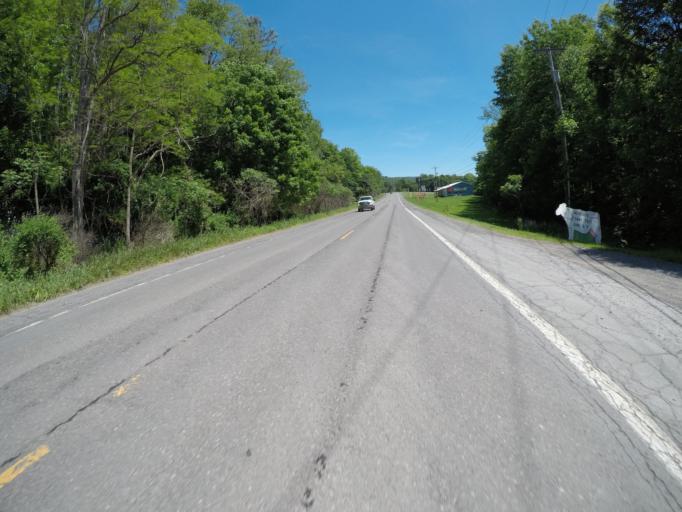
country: US
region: New York
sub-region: Delaware County
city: Delhi
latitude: 42.2067
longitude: -74.9826
